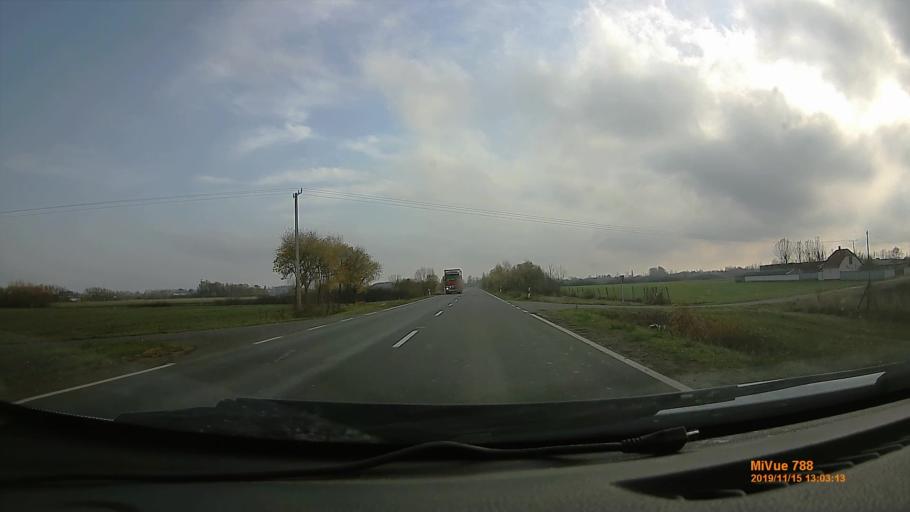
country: HU
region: Bekes
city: Gyula
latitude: 46.6452
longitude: 21.2425
